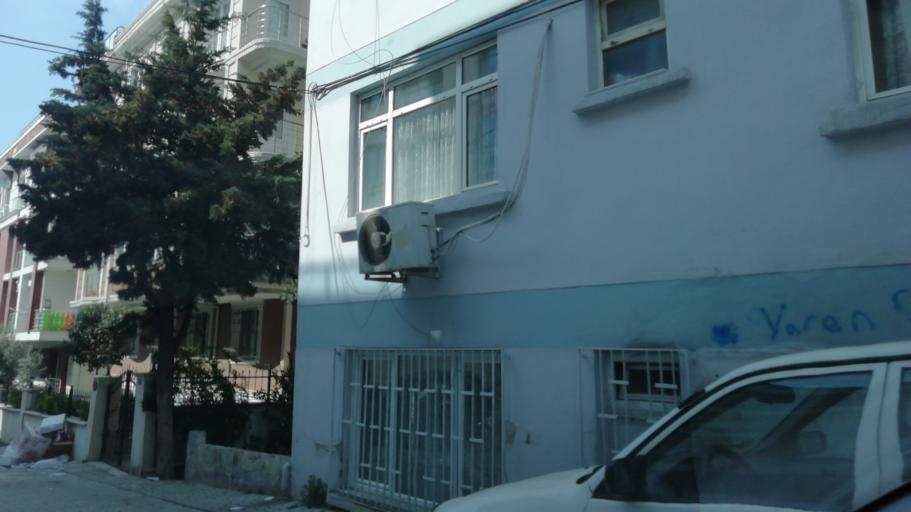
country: TR
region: Istanbul
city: Mahmutbey
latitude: 40.9960
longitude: 28.7694
